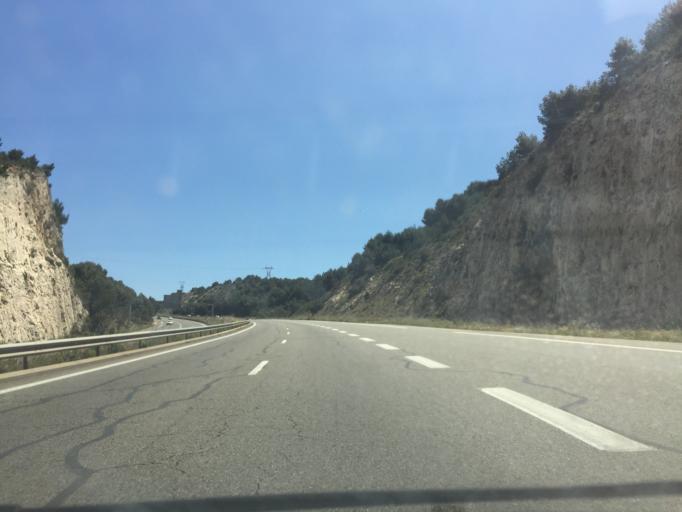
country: FR
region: Provence-Alpes-Cote d'Azur
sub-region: Departement des Bouches-du-Rhone
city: Les Pennes-Mirabeau
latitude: 43.3941
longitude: 5.2992
